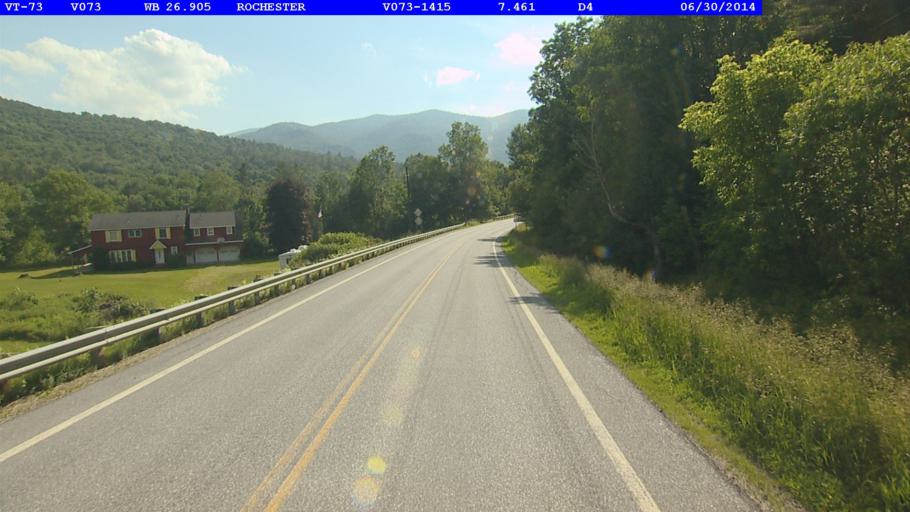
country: US
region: Vermont
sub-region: Orange County
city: Randolph
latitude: 43.8522
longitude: -72.8287
